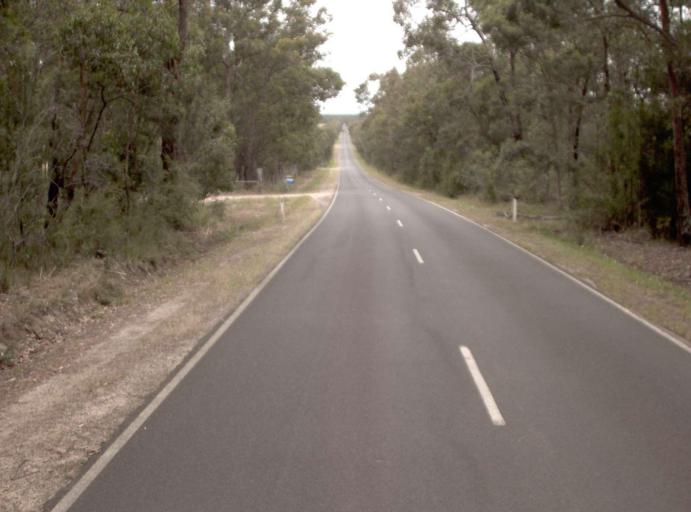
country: AU
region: Victoria
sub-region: Latrobe
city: Traralgon
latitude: -38.4761
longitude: 146.8219
